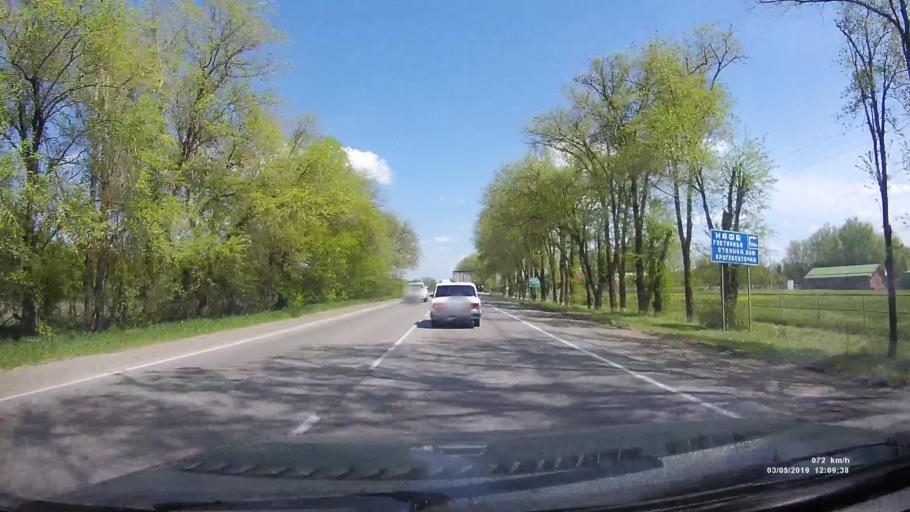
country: RU
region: Rostov
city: Bagayevskaya
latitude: 47.2957
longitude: 40.5188
